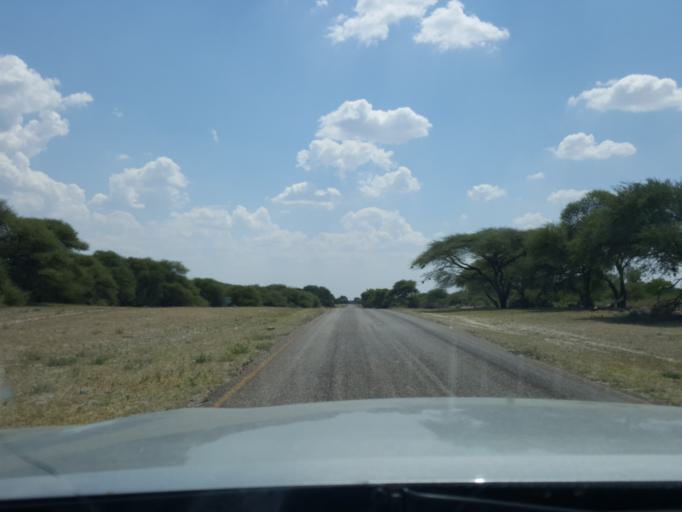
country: BW
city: Tsau
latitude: -20.1863
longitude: 22.4721
